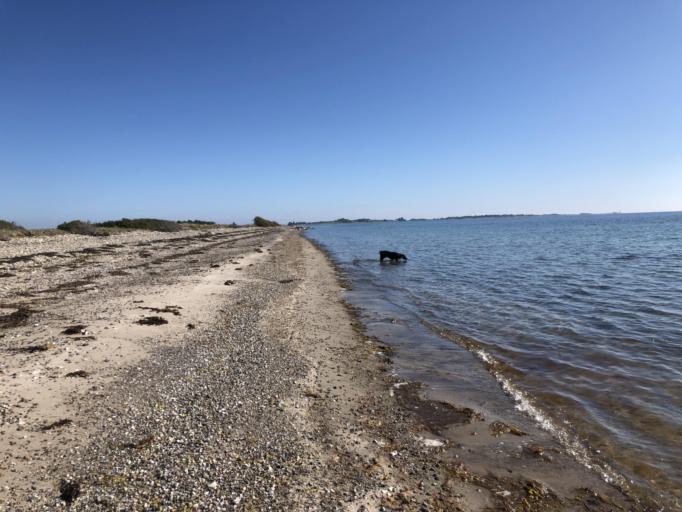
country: DK
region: Zealand
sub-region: Slagelse Kommune
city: Skaelskor
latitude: 55.2052
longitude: 11.1733
